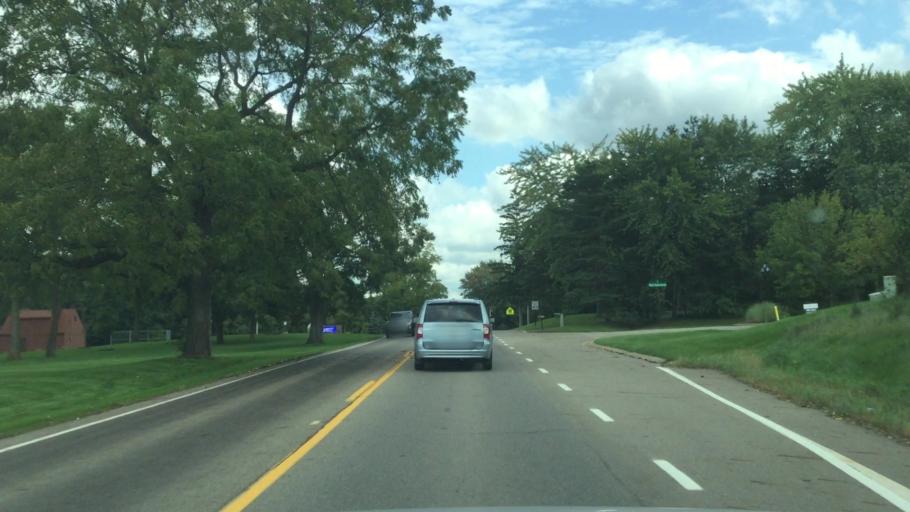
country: US
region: Michigan
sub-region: Livingston County
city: Brighton
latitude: 42.5520
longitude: -83.7642
